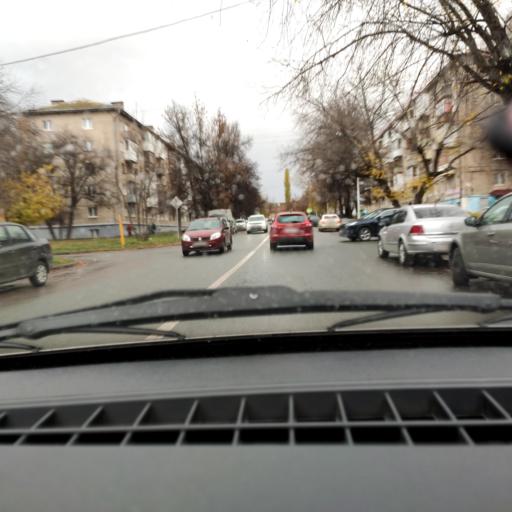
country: RU
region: Bashkortostan
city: Ufa
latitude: 54.8116
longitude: 56.1013
